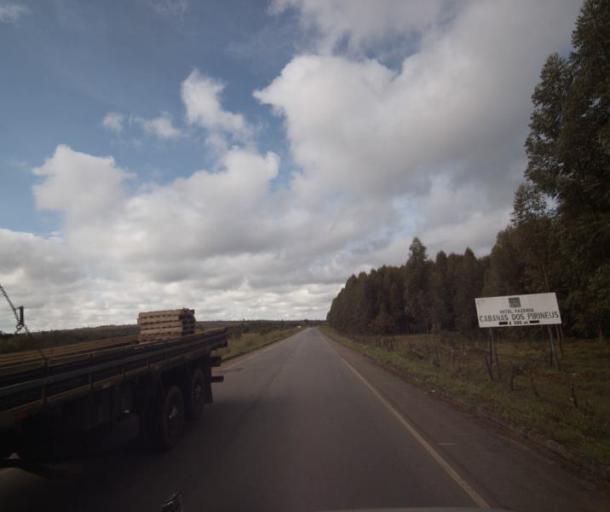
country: BR
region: Goias
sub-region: Pirenopolis
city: Pirenopolis
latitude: -15.8169
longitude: -48.7802
